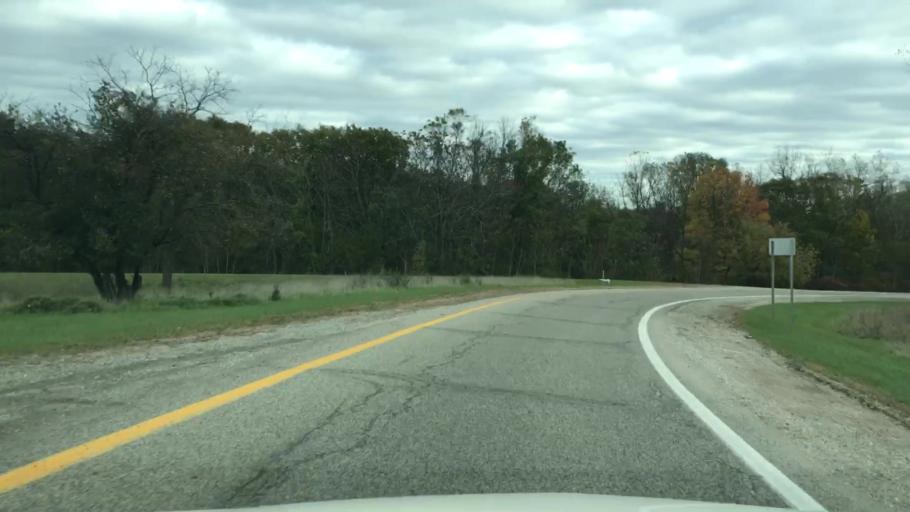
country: US
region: Michigan
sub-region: Macomb County
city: Shelby
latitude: 42.7073
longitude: -83.0705
